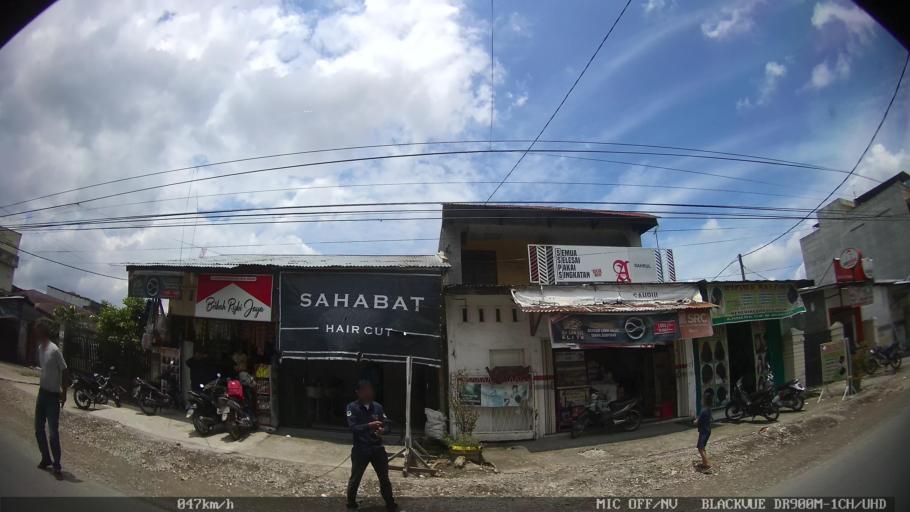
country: ID
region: North Sumatra
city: Medan
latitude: 3.6164
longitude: 98.6890
